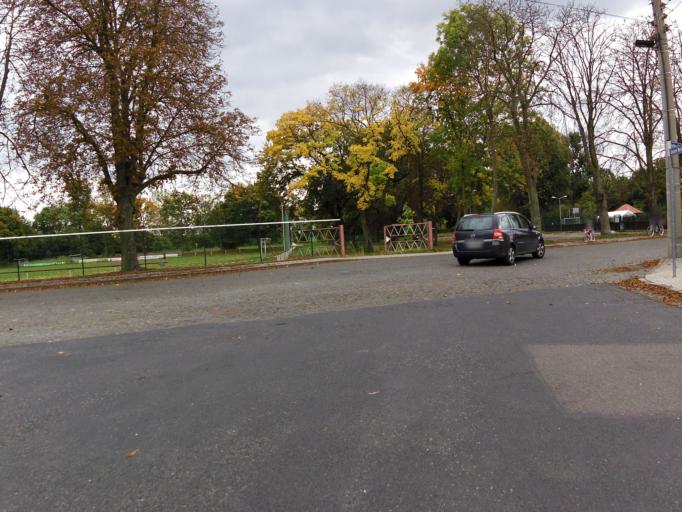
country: DE
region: Saxony
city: Grossposna
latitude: 51.3061
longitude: 12.4561
